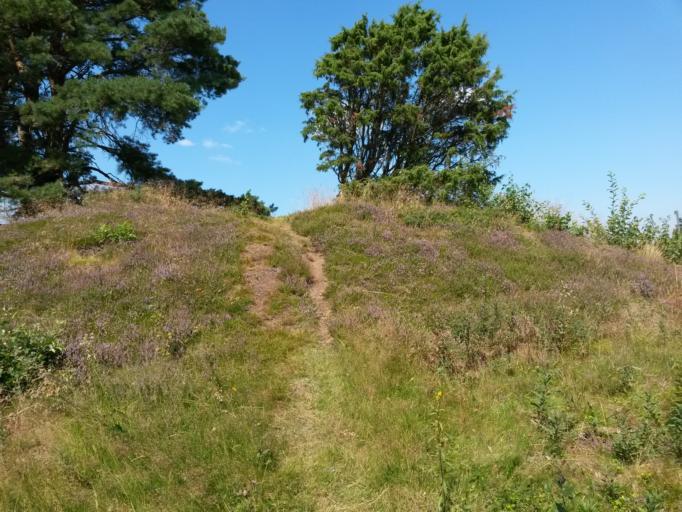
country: SE
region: Vaestra Goetaland
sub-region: Vargarda Kommun
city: Jonstorp
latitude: 57.9809
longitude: 12.6605
